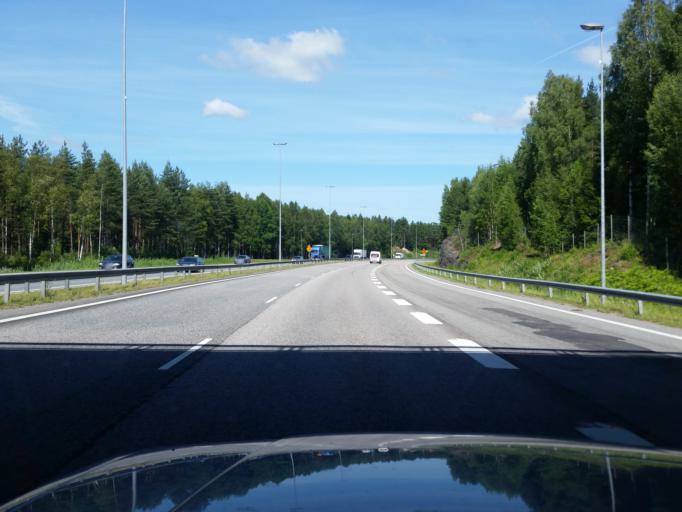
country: FI
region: Uusimaa
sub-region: Helsinki
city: Kirkkonummi
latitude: 60.2740
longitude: 24.4537
